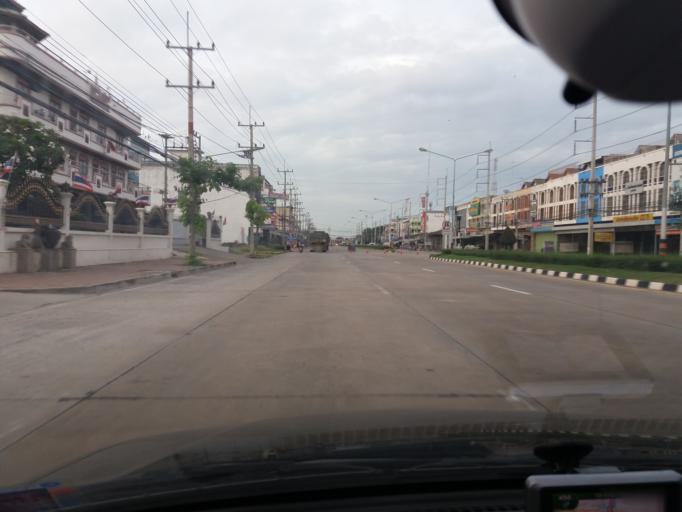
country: TH
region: Suphan Buri
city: U Thong
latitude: 14.3818
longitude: 99.8945
